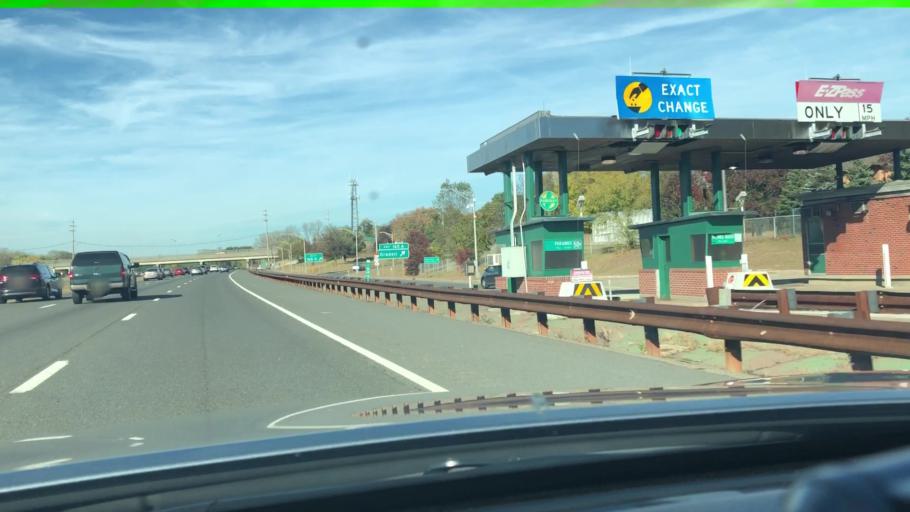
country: US
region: New Jersey
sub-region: Bergen County
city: Paramus
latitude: 40.9599
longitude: -74.0657
